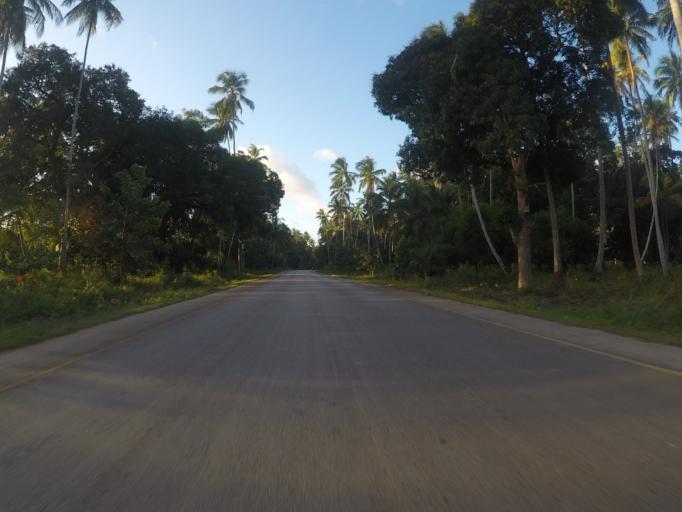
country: TZ
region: Zanzibar Central/South
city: Koani
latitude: -6.1526
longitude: 39.3296
